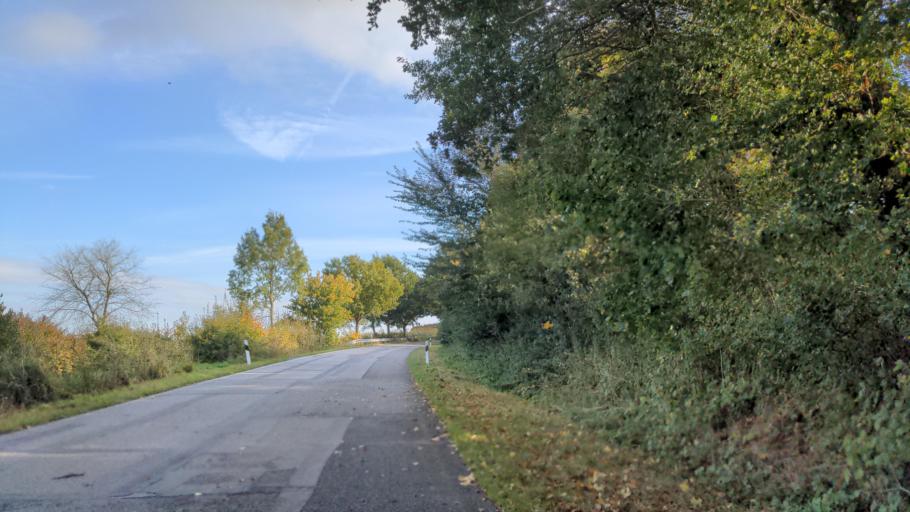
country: DE
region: Schleswig-Holstein
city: Damlos
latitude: 54.2384
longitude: 10.9135
